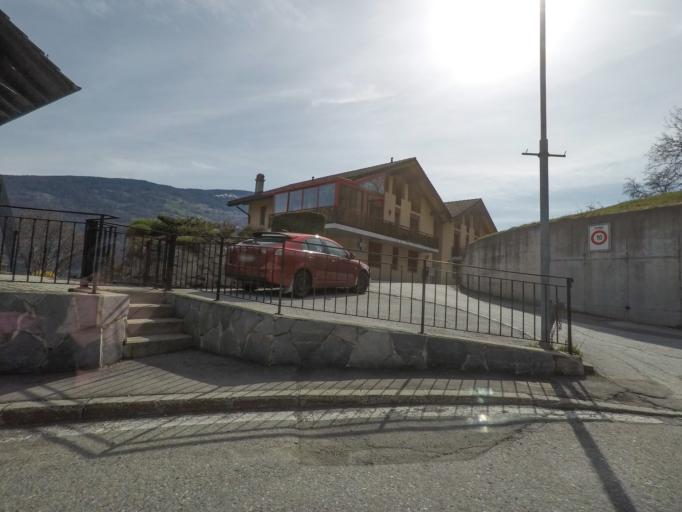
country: CH
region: Valais
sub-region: Herens District
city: Vex
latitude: 46.2106
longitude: 7.3974
